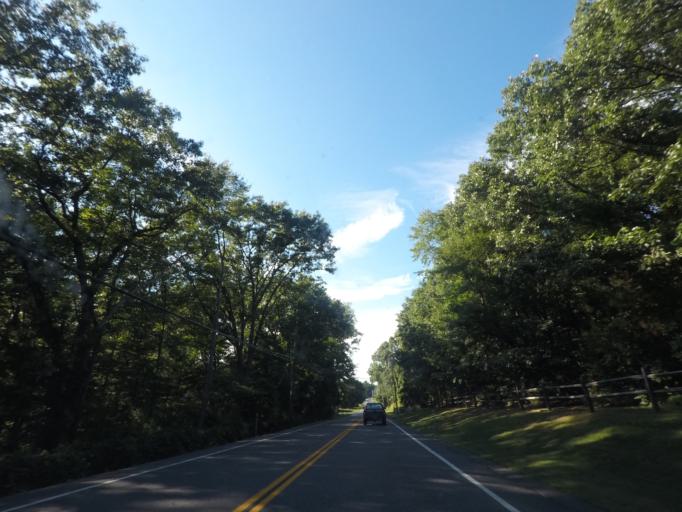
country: US
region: New York
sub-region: Albany County
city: West Albany
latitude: 42.7161
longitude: -73.7661
